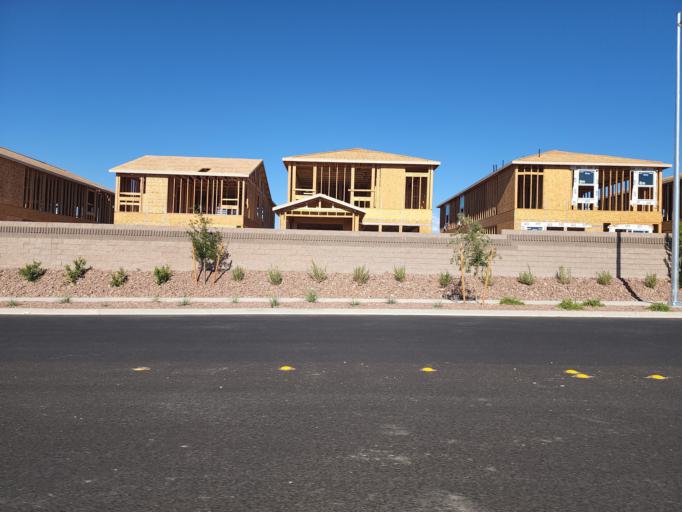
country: US
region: Nevada
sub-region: Clark County
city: Spring Valley
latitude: 36.0810
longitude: -115.2701
